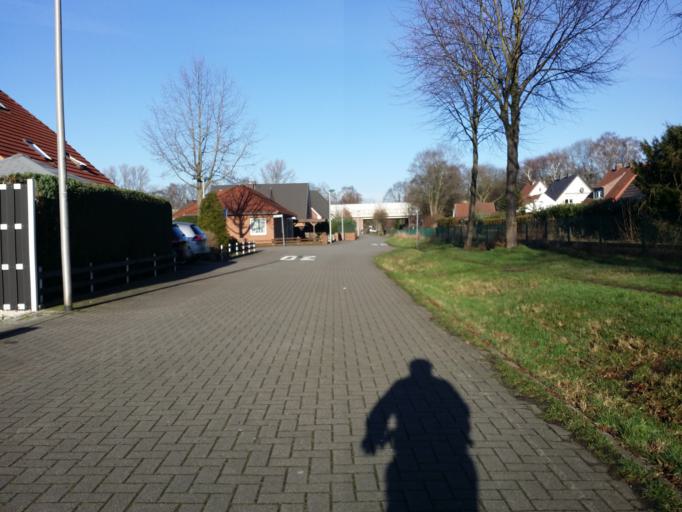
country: DE
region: Lower Saxony
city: Delmenhorst
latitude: 53.0298
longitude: 8.6446
